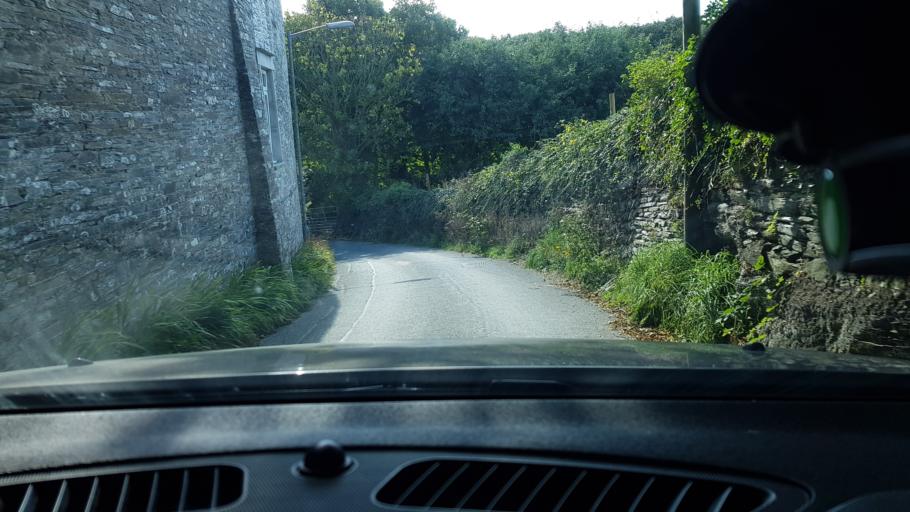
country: GB
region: England
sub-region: Cornwall
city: Tintagel
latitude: 50.6636
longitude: -4.7531
